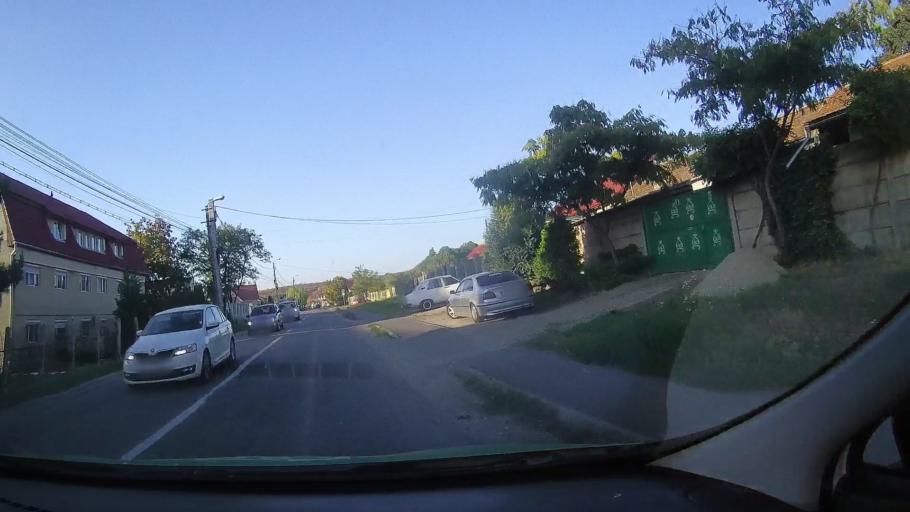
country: RO
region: Bihor
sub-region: Comuna Biharea
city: Oradea
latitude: 47.0893
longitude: 21.9265
